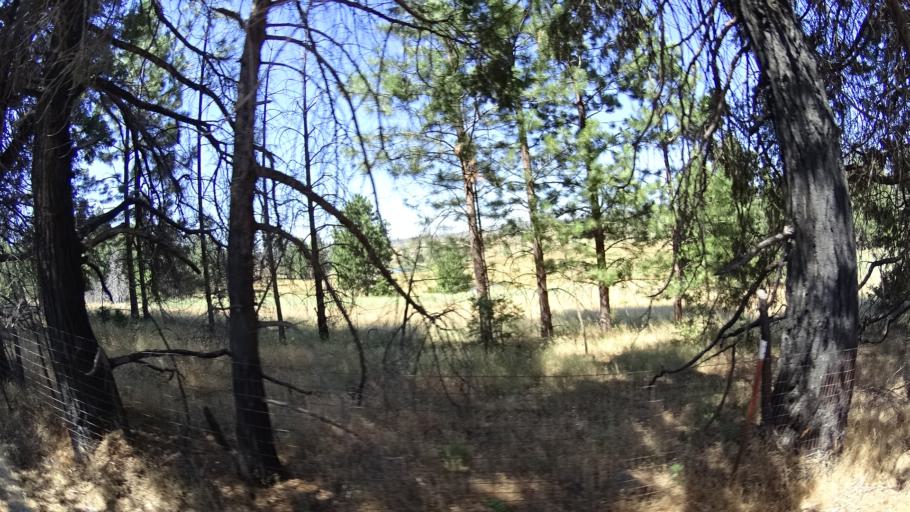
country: US
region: California
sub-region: Calaveras County
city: Mountain Ranch
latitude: 38.2829
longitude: -120.5281
